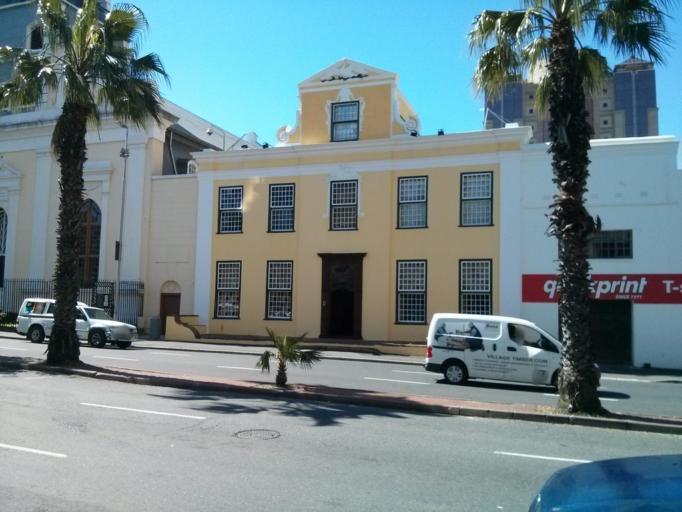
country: ZA
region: Western Cape
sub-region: City of Cape Town
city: Cape Town
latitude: -33.9195
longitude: 18.4199
